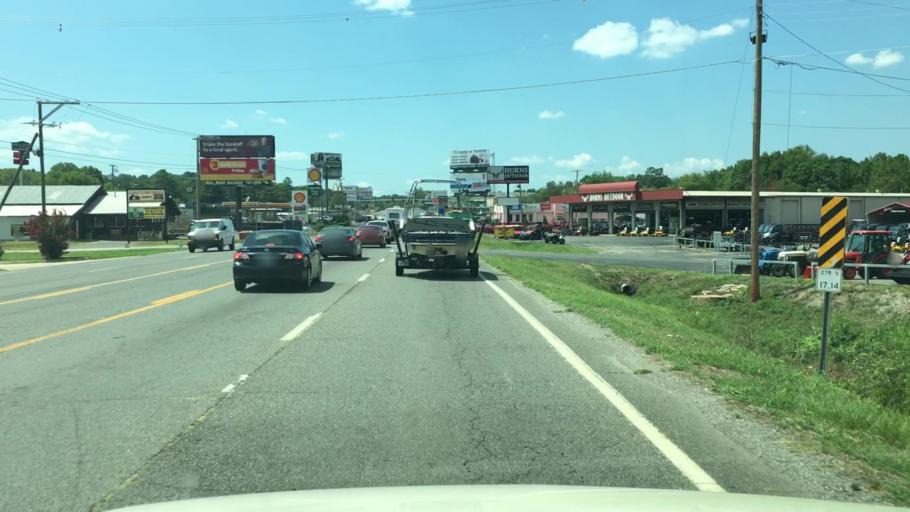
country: US
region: Arkansas
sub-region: Garland County
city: Piney
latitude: 34.5016
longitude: -93.1237
